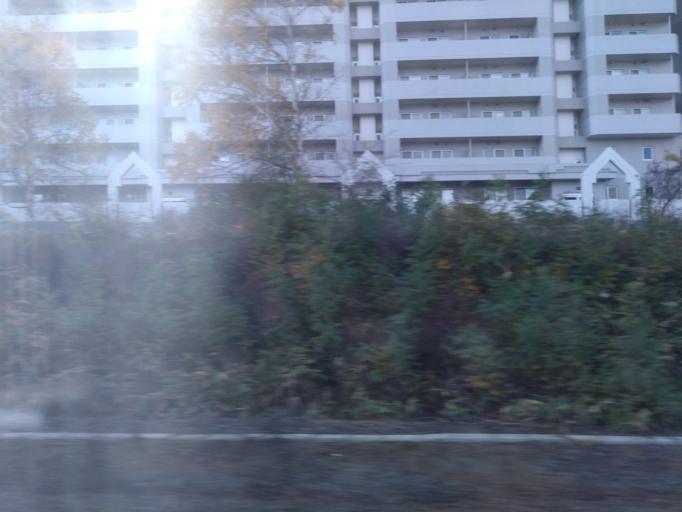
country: JP
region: Hokkaido
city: Kitahiroshima
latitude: 42.9828
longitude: 141.5628
